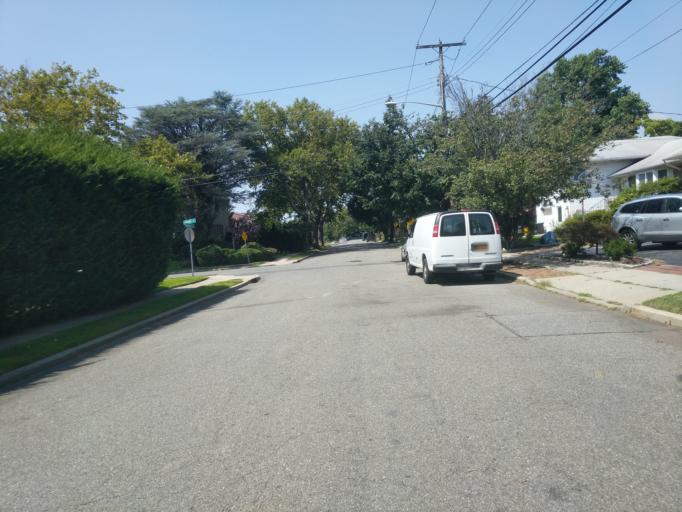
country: US
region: New York
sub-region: Nassau County
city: Woodmere
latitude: 40.6390
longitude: -73.7257
